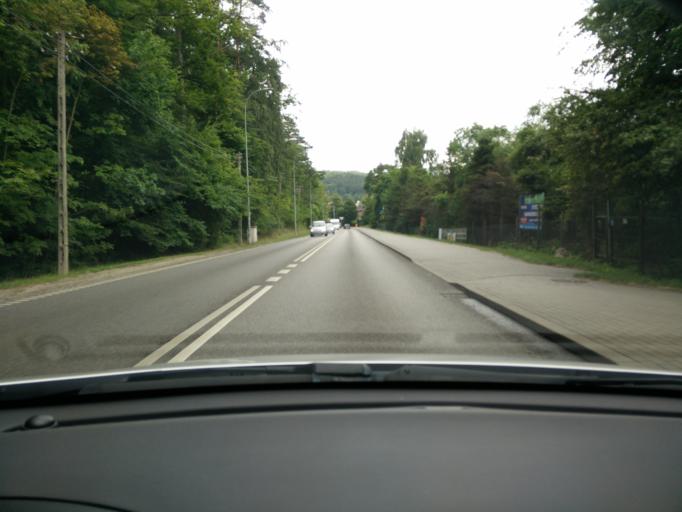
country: PL
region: Pomeranian Voivodeship
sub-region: Sopot
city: Sopot
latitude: 54.4138
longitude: 18.5471
